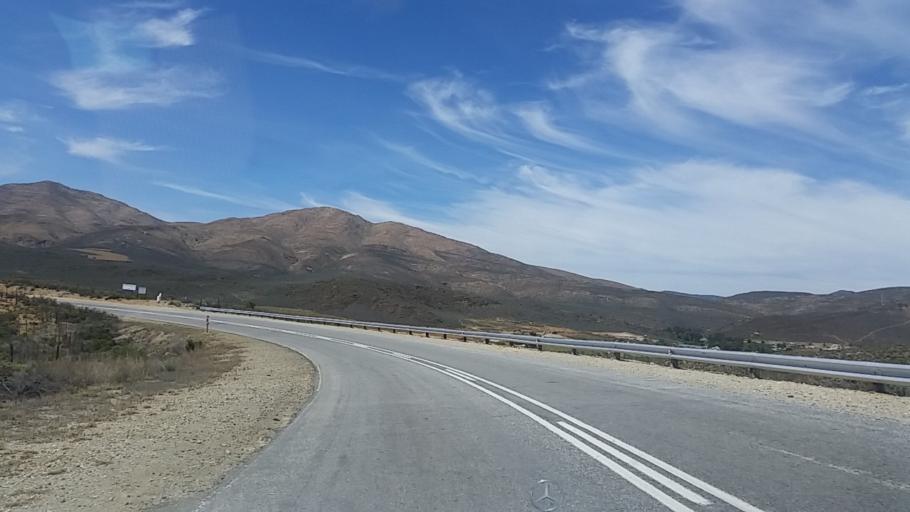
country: ZA
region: Western Cape
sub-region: Eden District Municipality
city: Knysna
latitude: -33.6393
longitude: 23.1299
